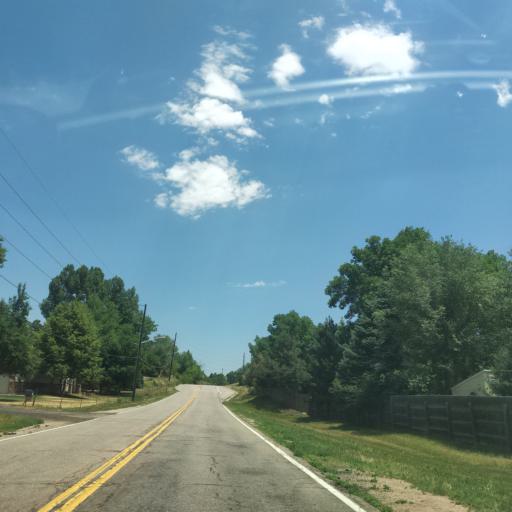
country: US
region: Colorado
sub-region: Jefferson County
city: Lakewood
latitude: 39.6743
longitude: -105.0894
